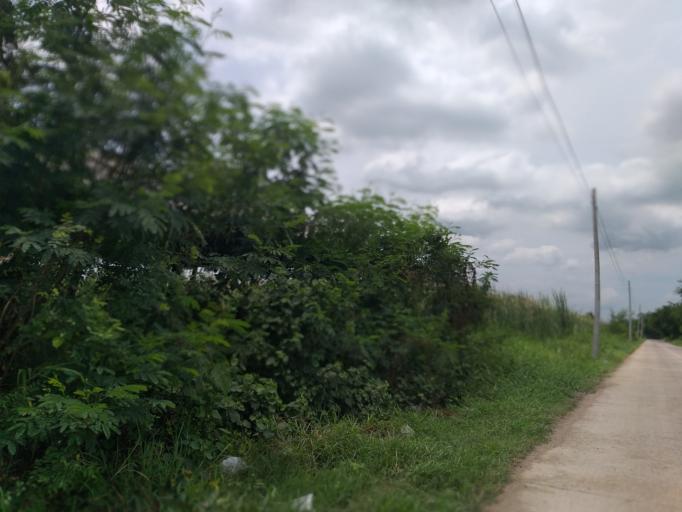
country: TH
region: Pathum Thani
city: Ban Lam Luk Ka
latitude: 13.9901
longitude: 100.8622
